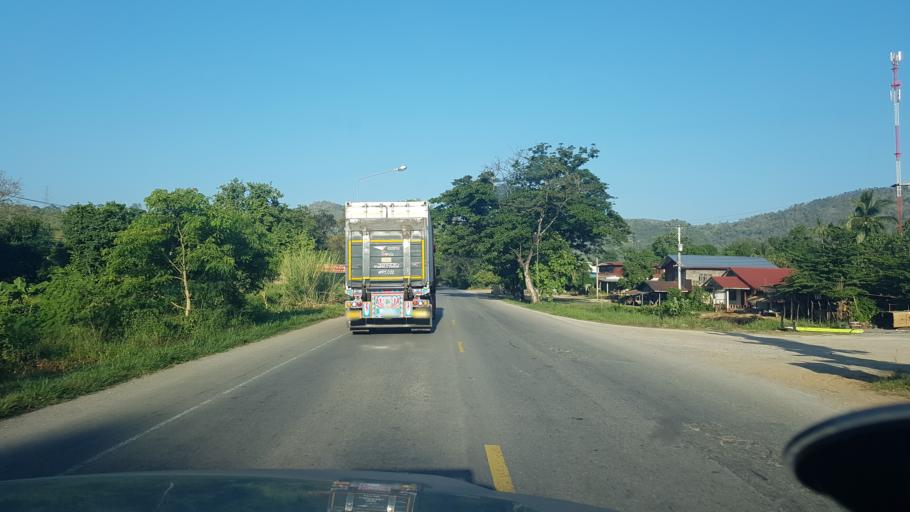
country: TH
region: Khon Kaen
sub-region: Amphoe Phu Pha Man
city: Phu Pha Man
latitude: 16.6460
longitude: 101.8180
